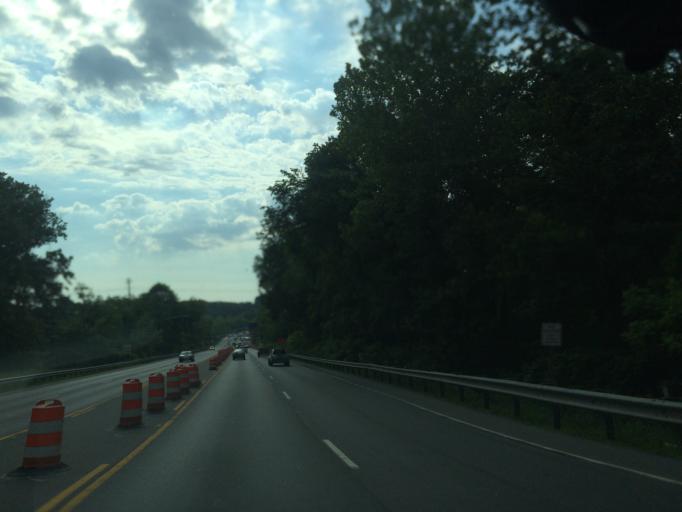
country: US
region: Maryland
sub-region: Baltimore County
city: Reisterstown
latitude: 39.4899
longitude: -76.8752
